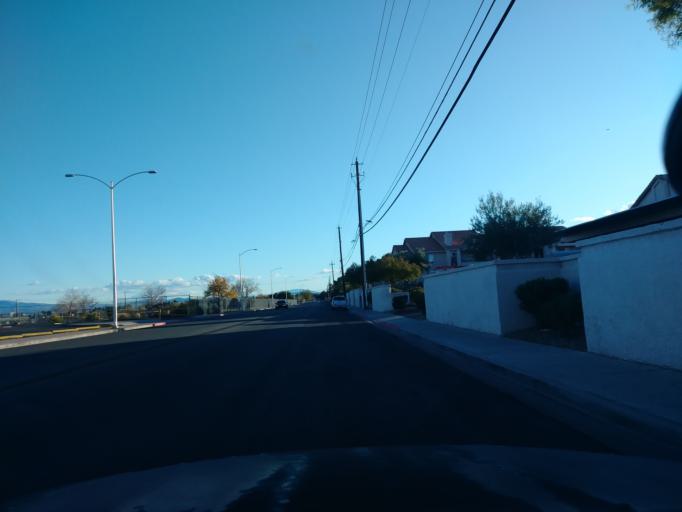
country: US
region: Nevada
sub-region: Clark County
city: Spring Valley
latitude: 36.1544
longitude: -115.2390
